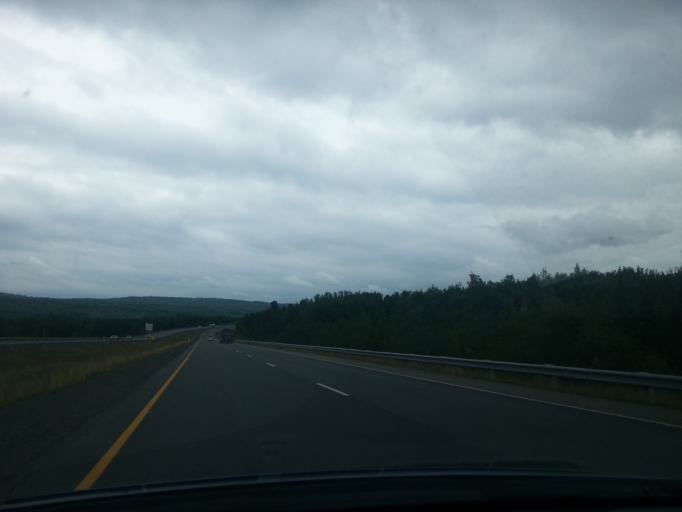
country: CA
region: New Brunswick
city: Harrison Brook
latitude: 47.2187
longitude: -67.9409
